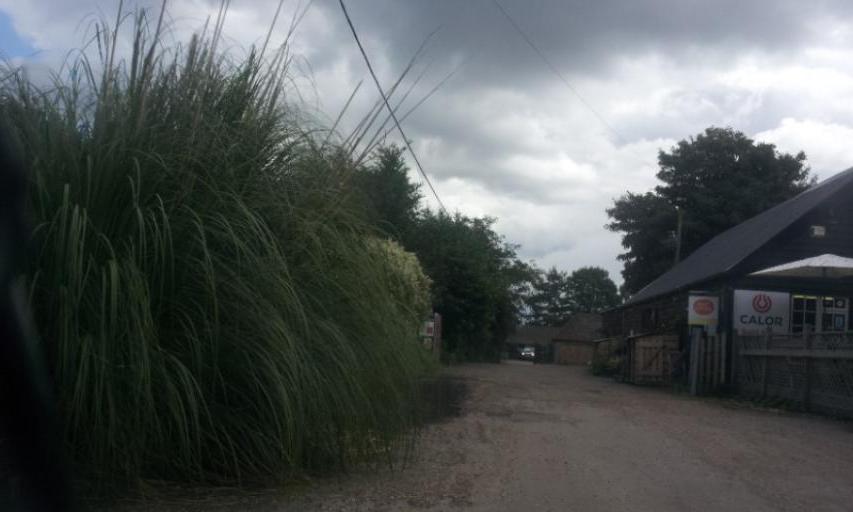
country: GB
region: England
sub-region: Kent
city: Sittingbourne
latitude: 51.3118
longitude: 0.6965
